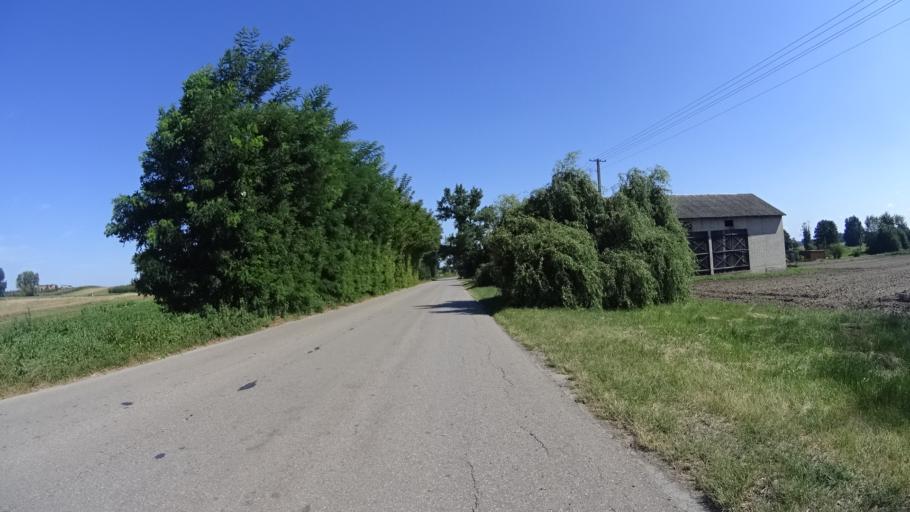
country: PL
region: Masovian Voivodeship
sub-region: Powiat bialobrzeski
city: Wysmierzyce
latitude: 51.6590
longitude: 20.8276
